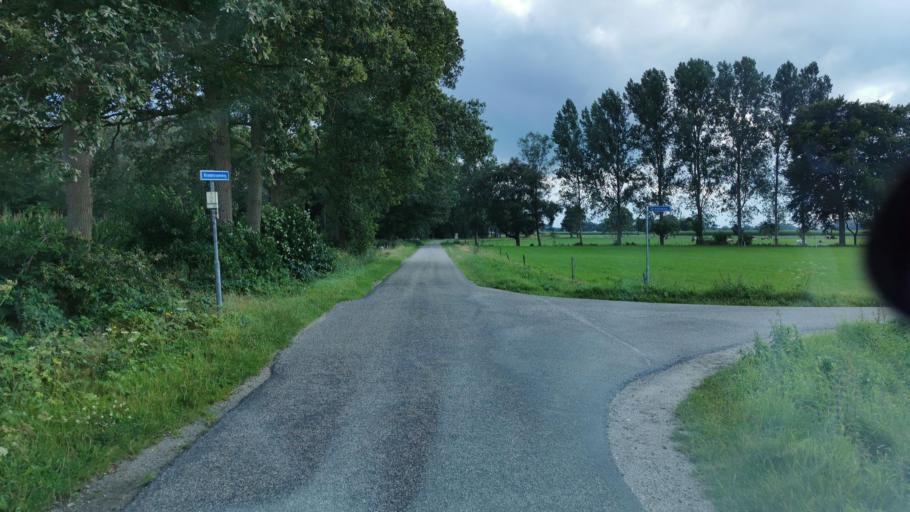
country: NL
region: Overijssel
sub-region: Gemeente Losser
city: Losser
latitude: 52.2431
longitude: 6.9889
